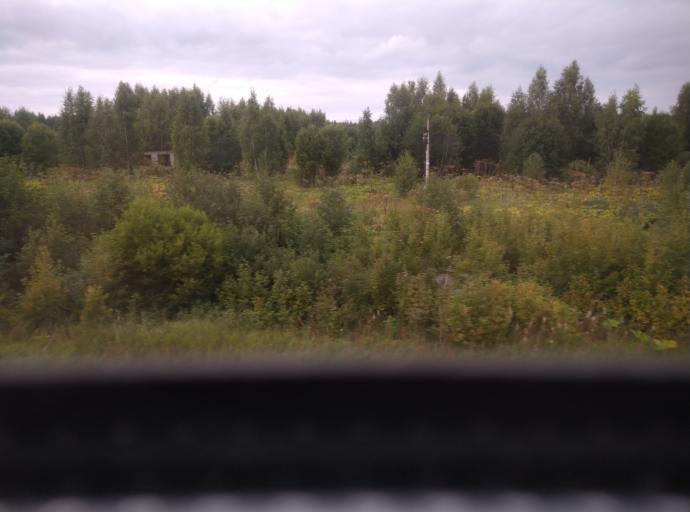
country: RU
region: Jaroslavl
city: Burmakino
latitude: 57.4389
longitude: 40.3943
